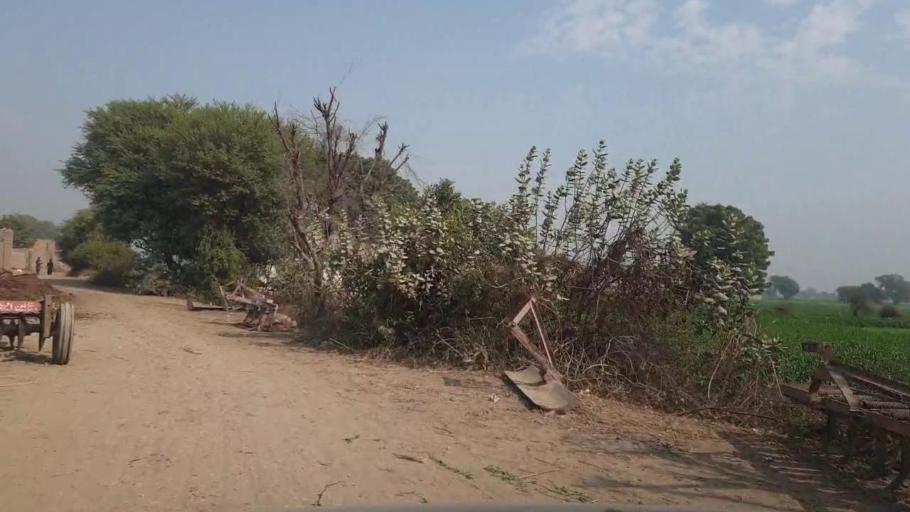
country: PK
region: Sindh
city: Hala
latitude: 25.7712
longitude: 68.4488
